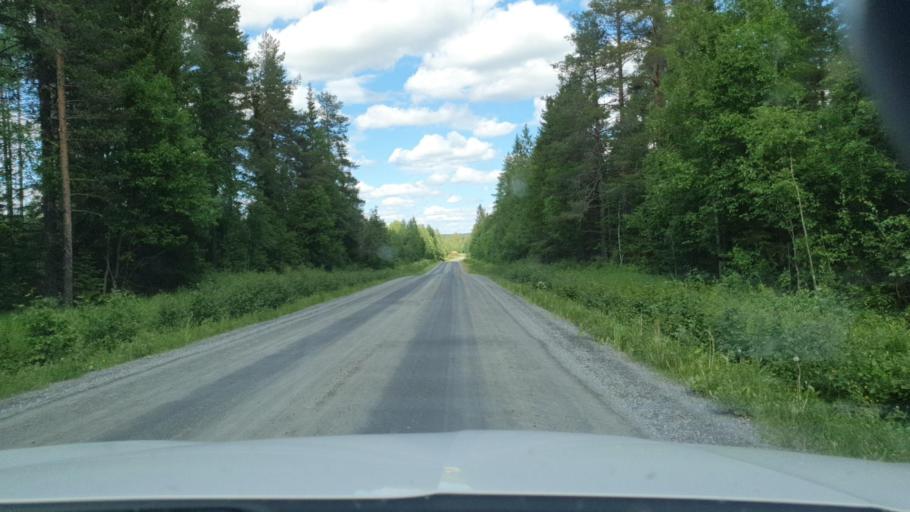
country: SE
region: Vaesterbotten
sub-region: Skelleftea Kommun
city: Forsbacka
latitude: 64.8364
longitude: 20.5037
